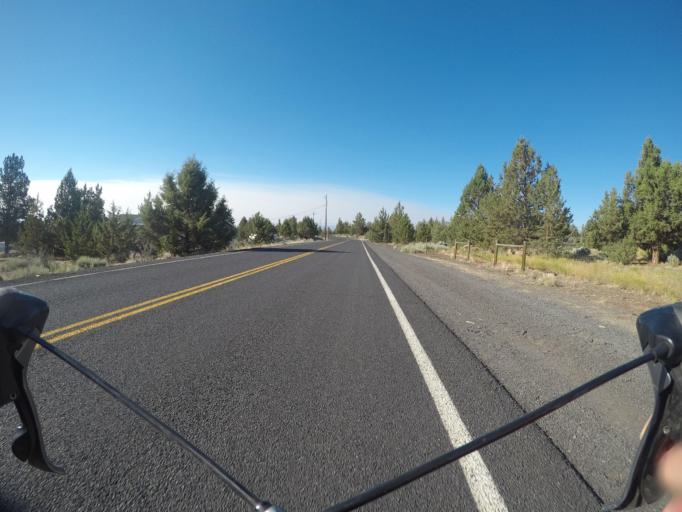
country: US
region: Oregon
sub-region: Deschutes County
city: Bend
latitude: 44.1739
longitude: -121.2662
